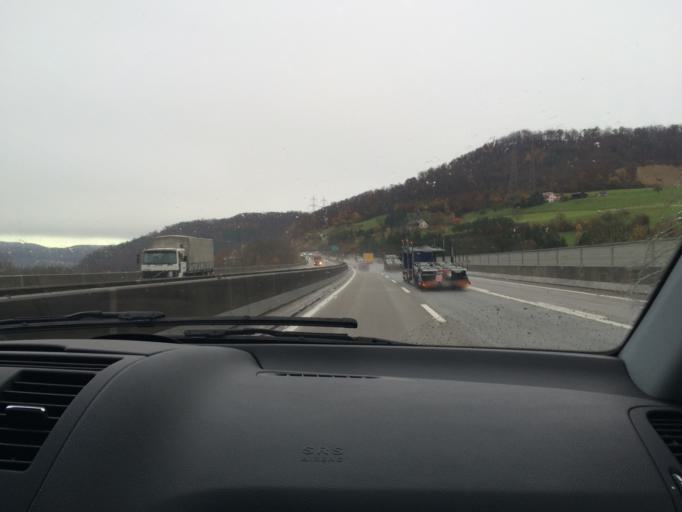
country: CH
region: Basel-Landschaft
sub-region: Bezirk Sissach
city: Itingen
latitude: 47.4690
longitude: 7.7955
